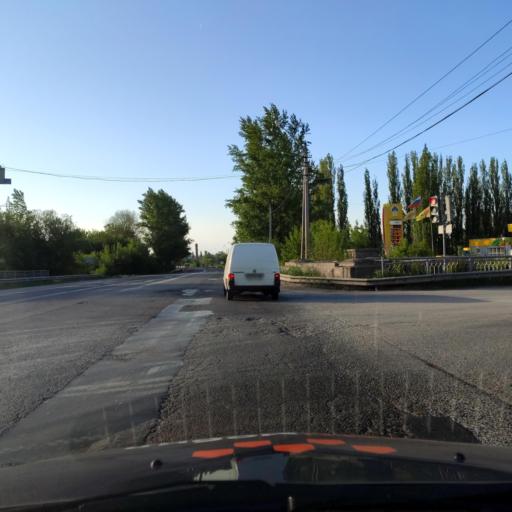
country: RU
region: Lipetsk
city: Yelets
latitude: 52.5999
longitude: 38.4732
